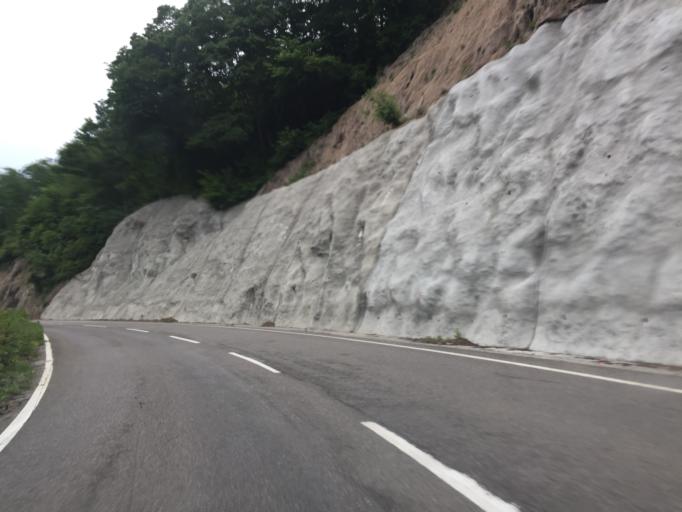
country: JP
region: Fukushima
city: Namie
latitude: 37.4126
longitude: 140.8308
